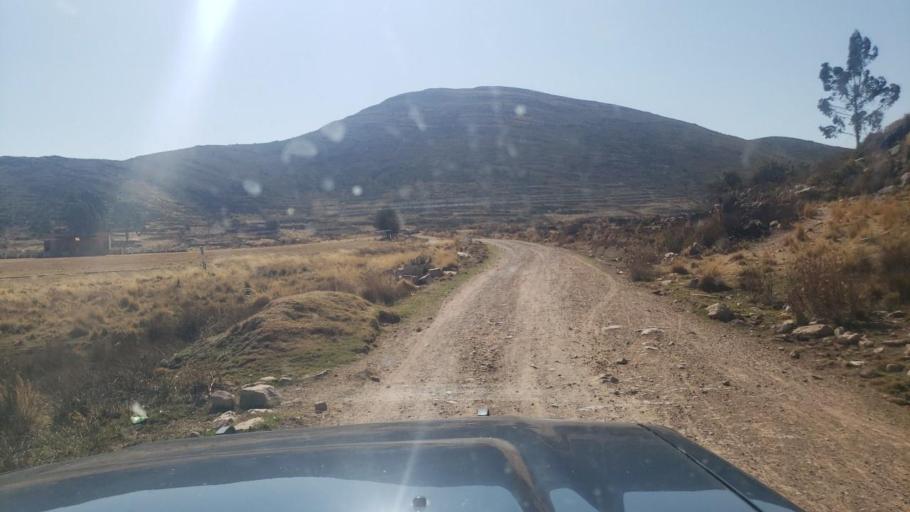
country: BO
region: La Paz
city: Huatajata
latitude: -16.3366
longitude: -68.6784
